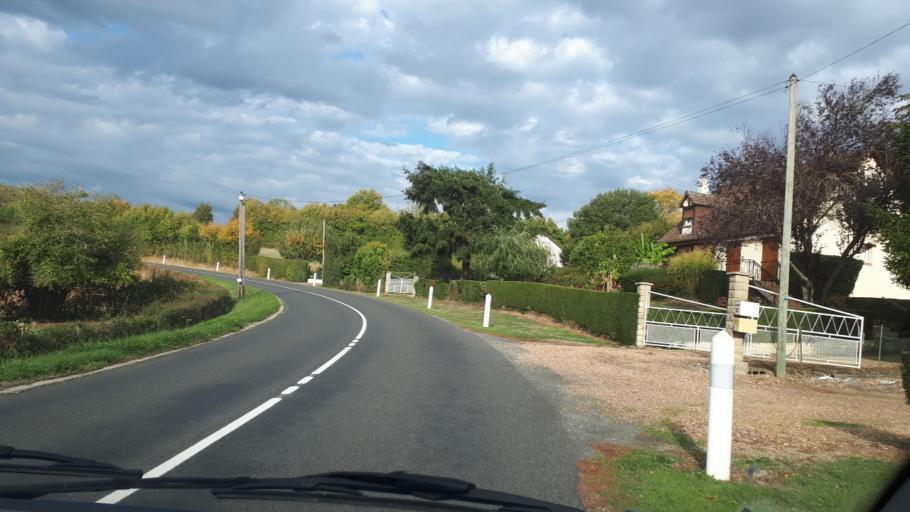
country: FR
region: Centre
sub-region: Departement du Loir-et-Cher
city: Mondoubleau
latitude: 47.9763
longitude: 0.9097
